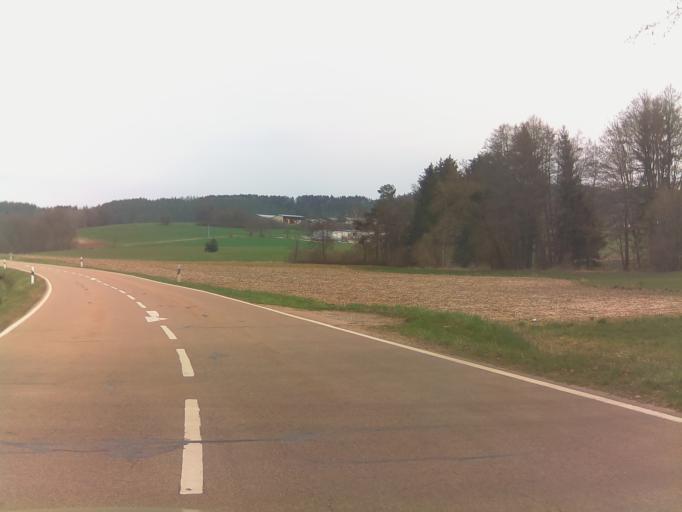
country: DE
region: Bavaria
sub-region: Upper Palatinate
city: Hahnbach
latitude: 49.5589
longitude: 11.8042
